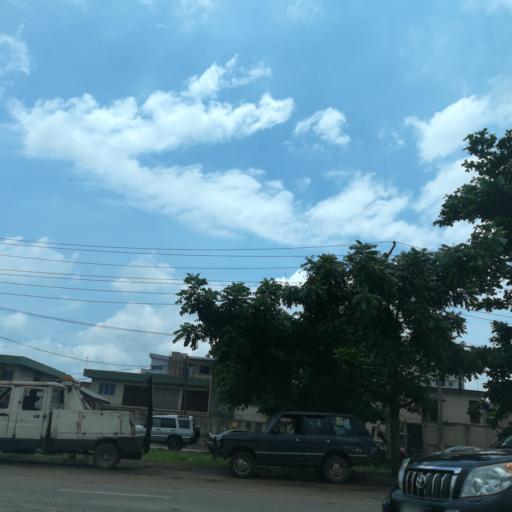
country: NG
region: Lagos
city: Somolu
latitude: 6.5583
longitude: 3.3637
